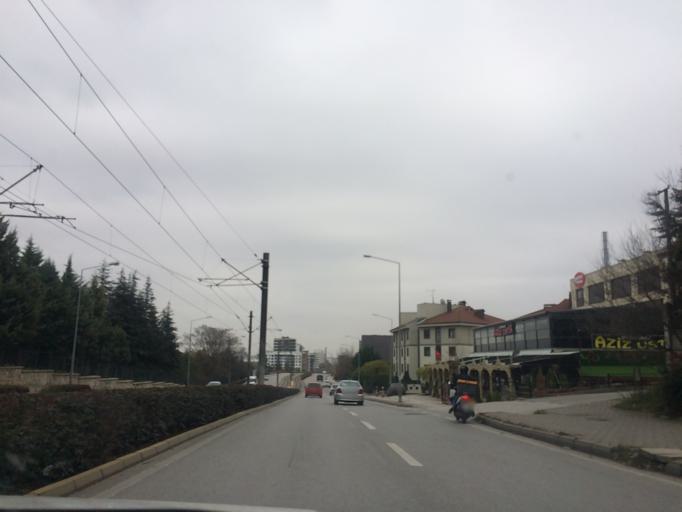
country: TR
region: Eskisehir
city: Eskisehir
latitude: 39.7885
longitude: 30.4934
